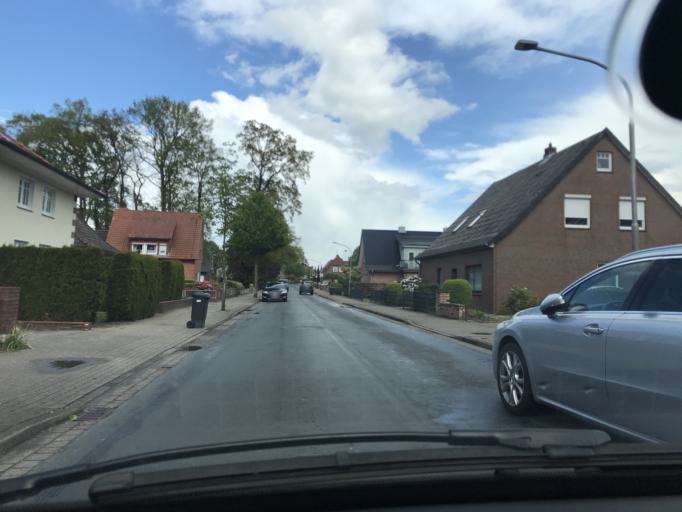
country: DE
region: Lower Saxony
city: Harsefeld
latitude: 53.4612
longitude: 9.5109
